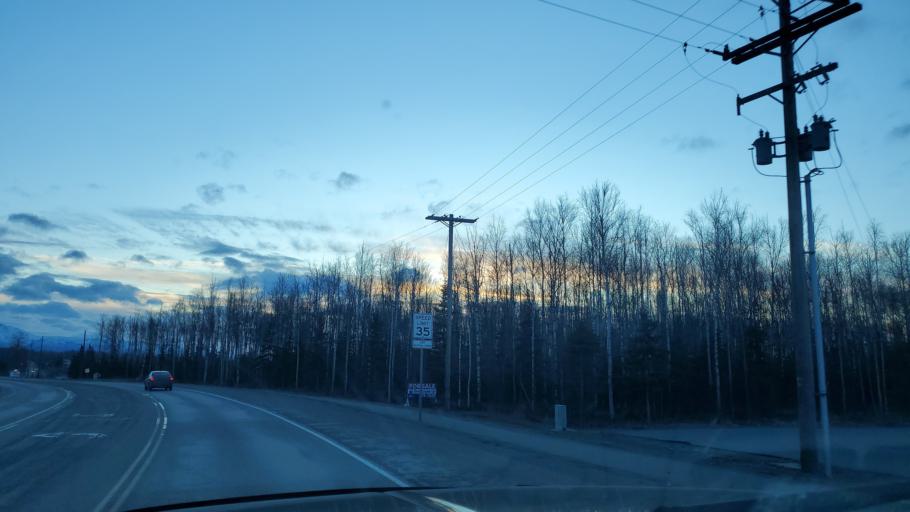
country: US
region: Alaska
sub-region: Matanuska-Susitna Borough
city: Wasilla
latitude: 61.5888
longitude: -149.4435
